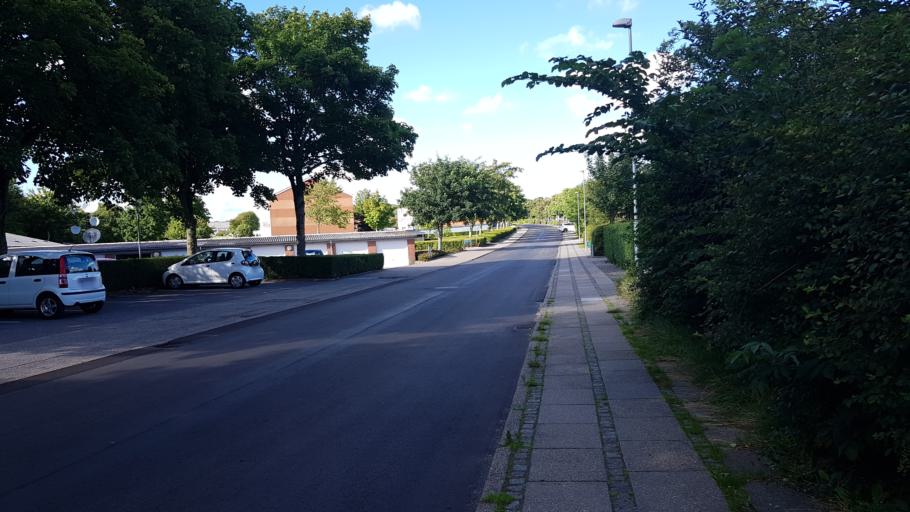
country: DK
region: North Denmark
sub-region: Thisted Kommune
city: Thisted
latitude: 56.9612
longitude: 8.6969
